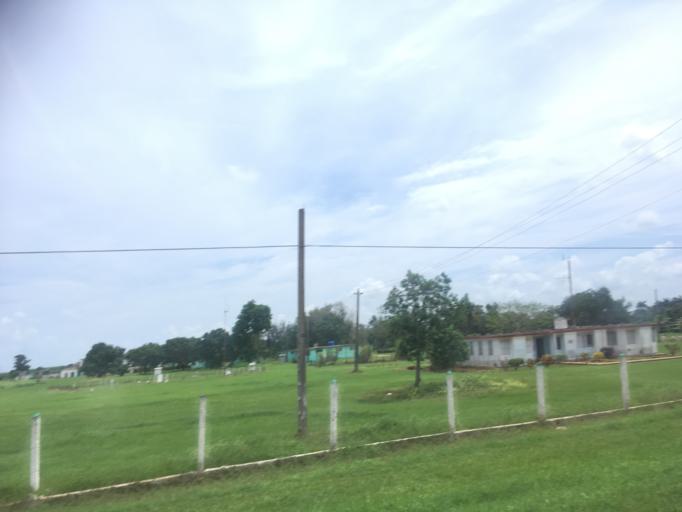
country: CU
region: Matanzas
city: Jovellanos
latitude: 22.7963
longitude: -81.1443
